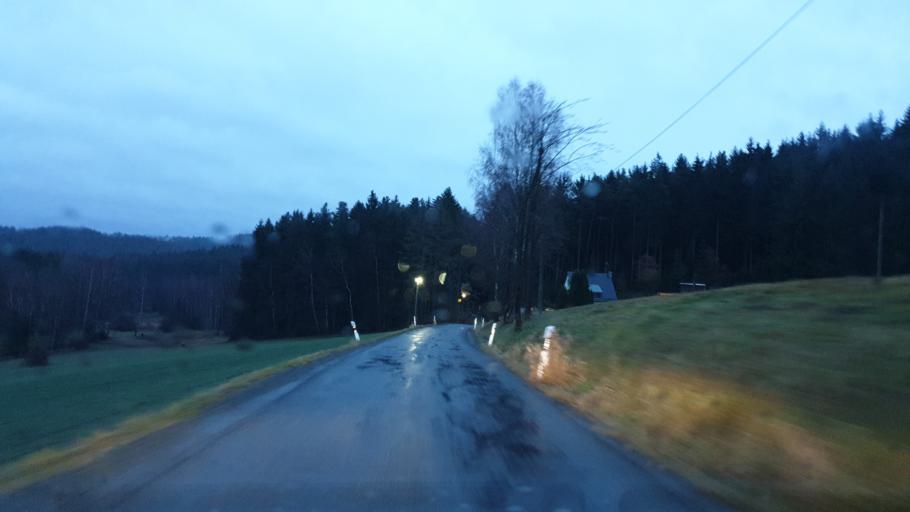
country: DE
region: Saxony
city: Bad Elster
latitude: 50.3062
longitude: 12.2372
